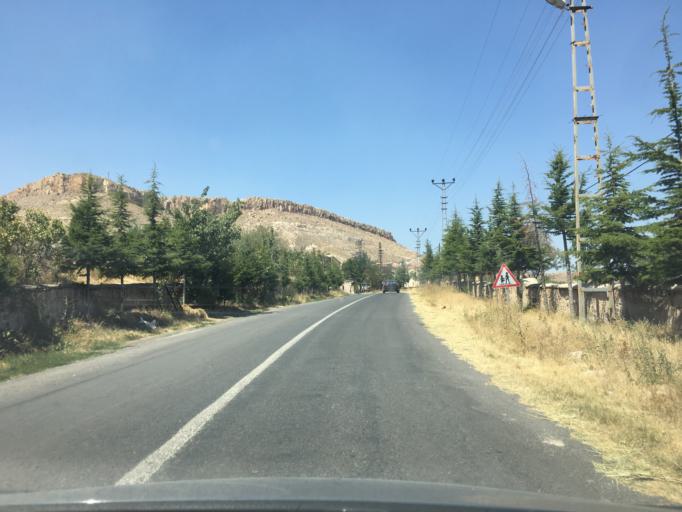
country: TR
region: Nevsehir
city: Urgub
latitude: 38.4693
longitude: 34.9518
